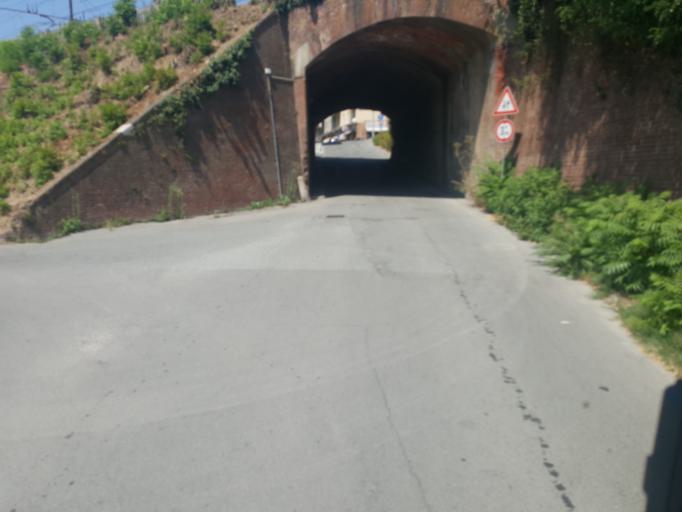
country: IT
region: Piedmont
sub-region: Provincia di Alessandria
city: Acqui Terme
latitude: 44.6723
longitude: 8.4784
